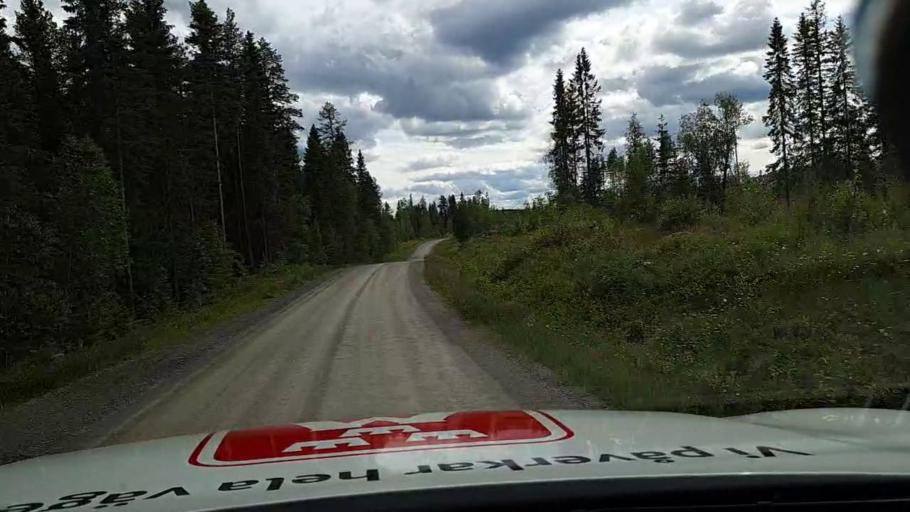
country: SE
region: Jaemtland
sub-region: Braecke Kommun
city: Braecke
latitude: 63.2691
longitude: 15.3779
